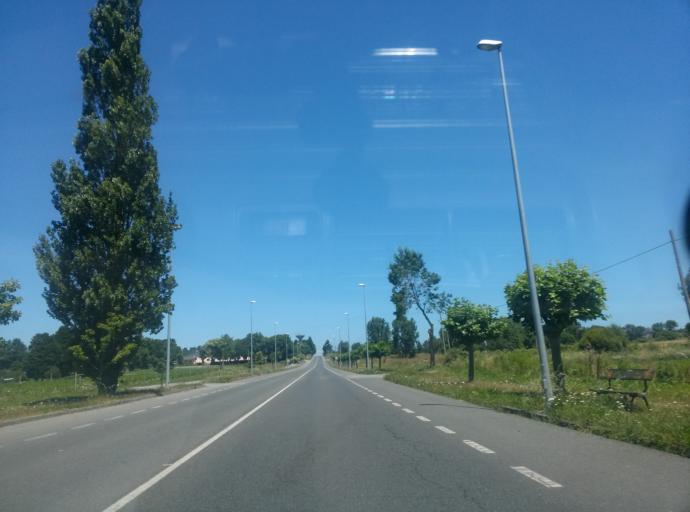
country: ES
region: Galicia
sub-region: Provincia de Lugo
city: Mos
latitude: 43.1517
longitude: -7.4884
